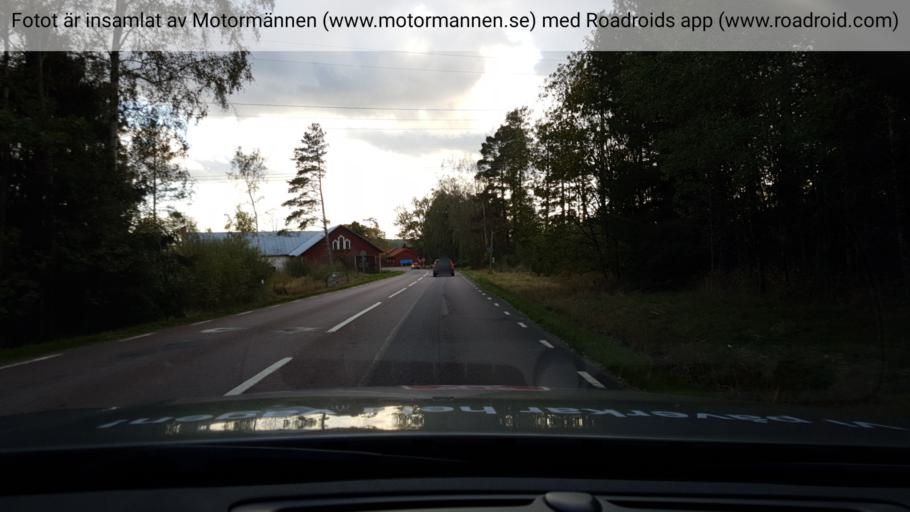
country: SE
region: Vaermland
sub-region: Karlstads Kommun
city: Skattkarr
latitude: 59.4200
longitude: 13.8303
